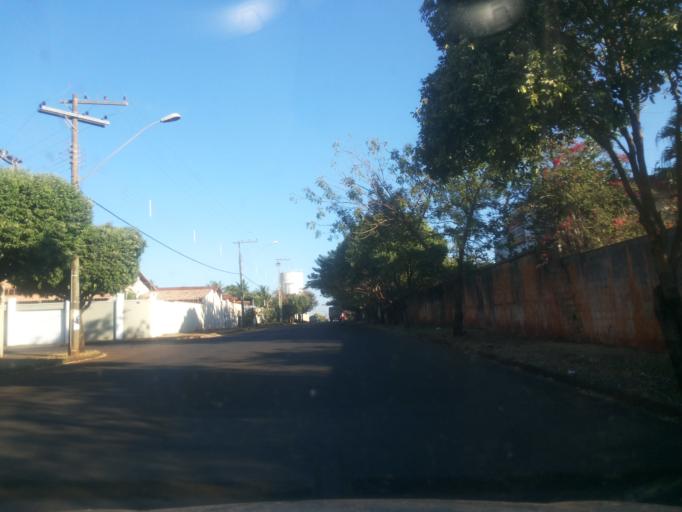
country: BR
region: Minas Gerais
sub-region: Ituiutaba
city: Ituiutaba
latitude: -18.9928
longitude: -49.4553
